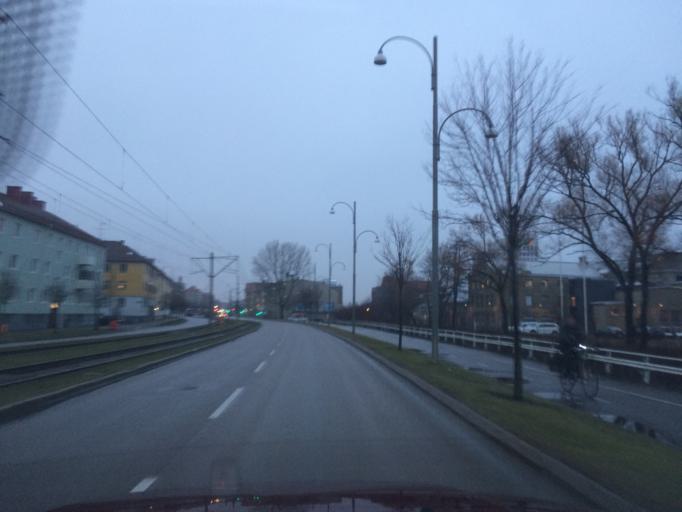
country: SE
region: Vaestra Goetaland
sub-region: Molndal
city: Moelndal
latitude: 57.6851
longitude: 11.9995
